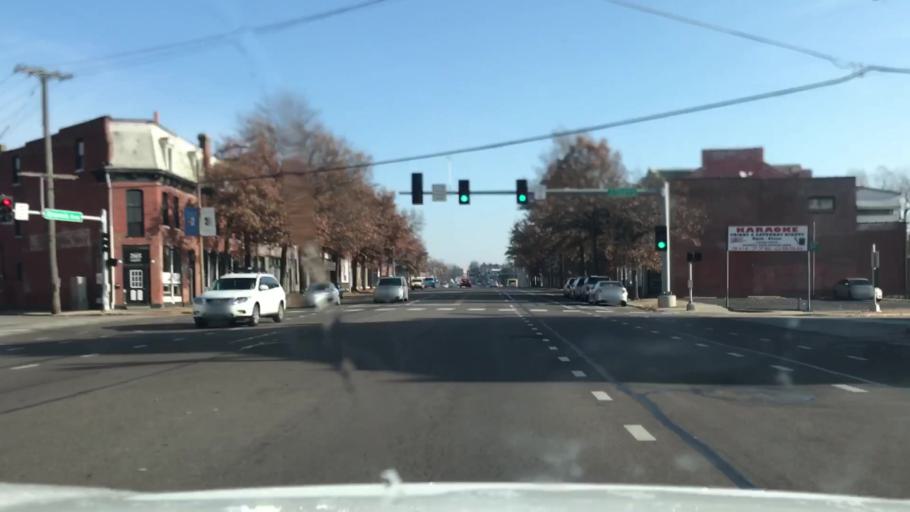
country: US
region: Missouri
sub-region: City of Saint Louis
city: St. Louis
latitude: 38.6037
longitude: -90.2258
